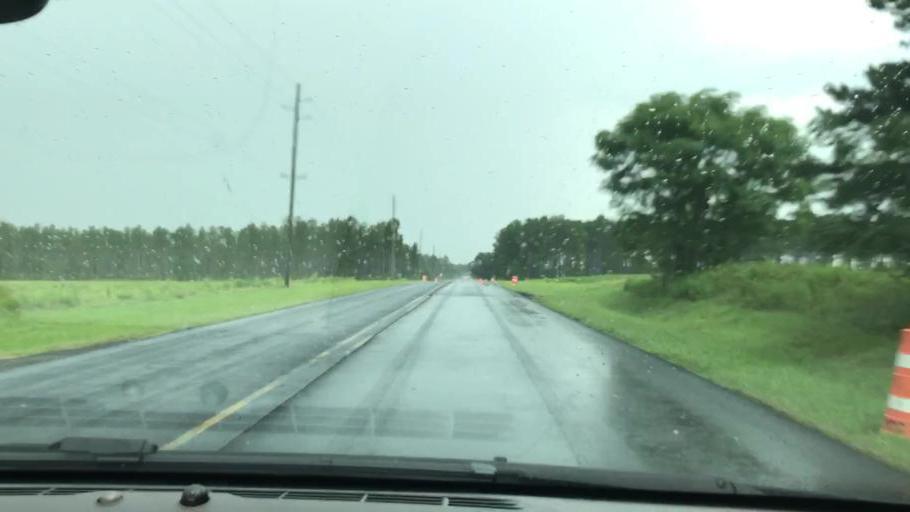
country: US
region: Georgia
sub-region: Clay County
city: Fort Gaines
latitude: 31.5308
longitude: -85.0217
